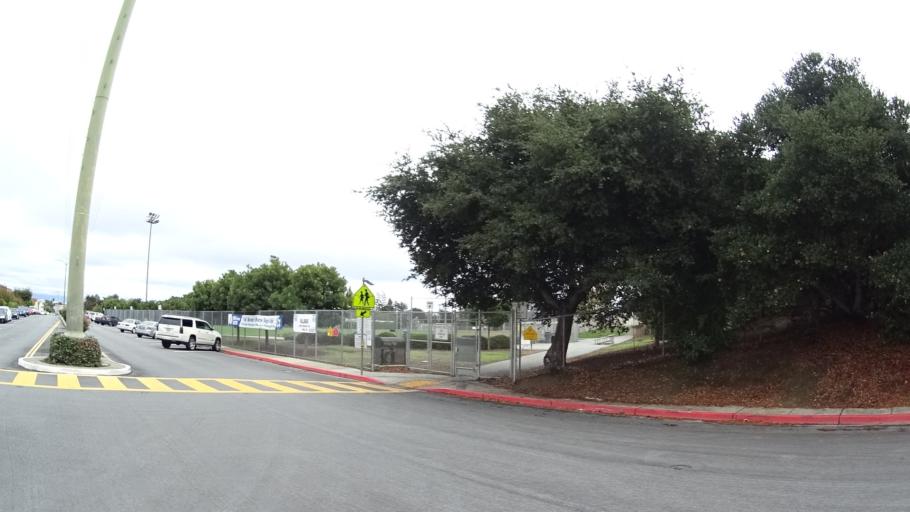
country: US
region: California
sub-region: San Mateo County
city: Millbrae
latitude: 37.5996
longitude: -122.4043
